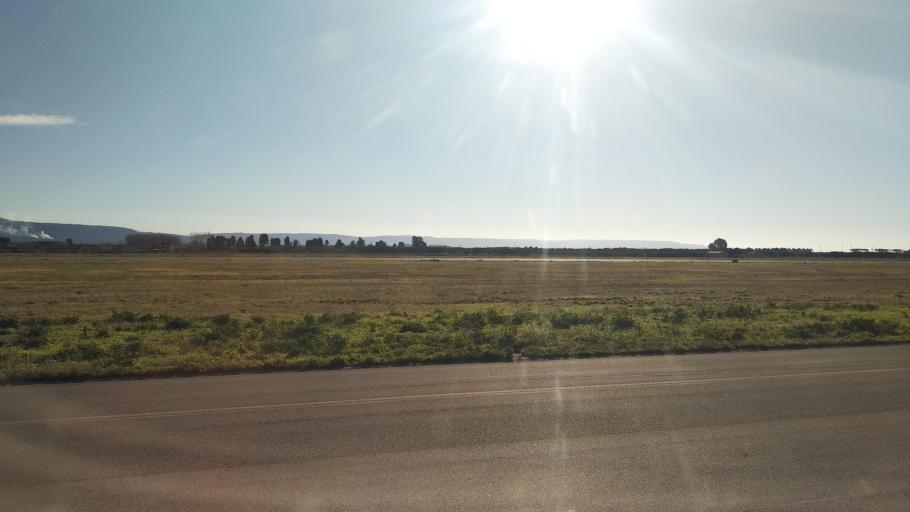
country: IT
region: Calabria
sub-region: Provincia di Catanzaro
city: Santa Eufemia Lamezia
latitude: 38.9072
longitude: 16.2465
